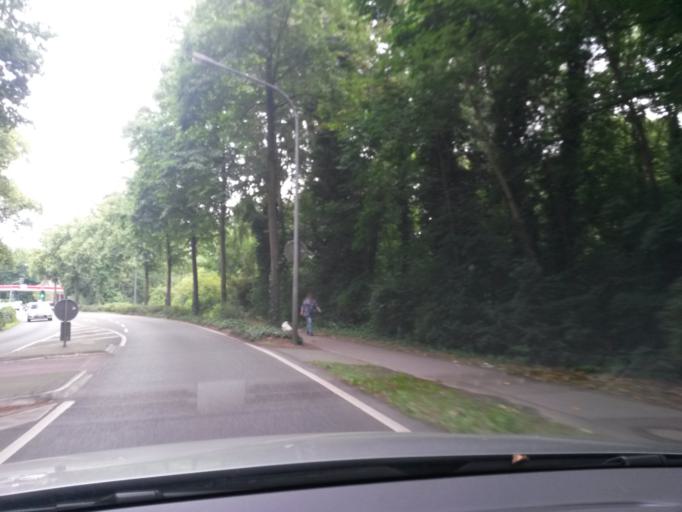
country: DE
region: North Rhine-Westphalia
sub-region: Regierungsbezirk Dusseldorf
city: Viersen
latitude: 51.2862
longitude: 6.3827
